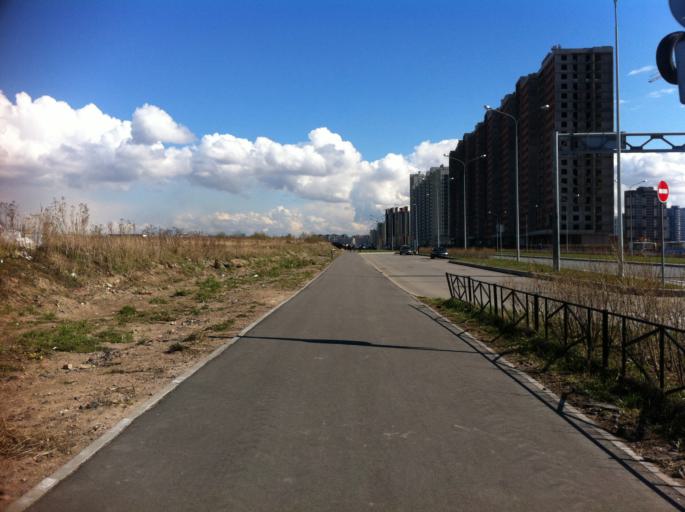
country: RU
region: St.-Petersburg
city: Uritsk
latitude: 59.8685
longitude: 30.1703
